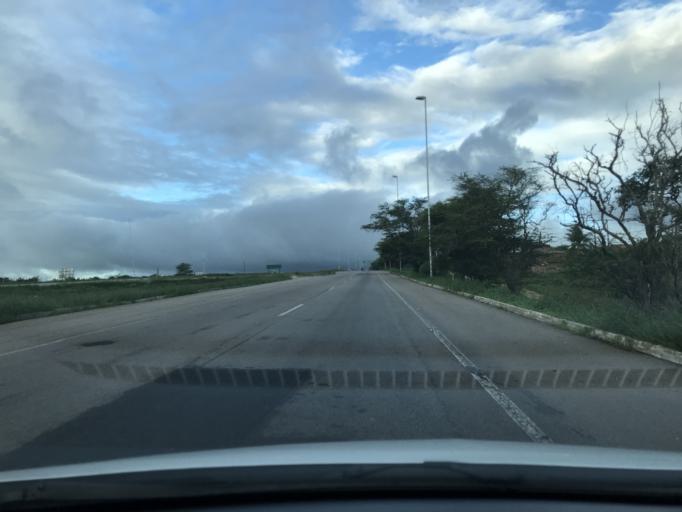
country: BR
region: Pernambuco
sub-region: Bezerros
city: Bezerros
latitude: -8.2990
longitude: -35.8563
